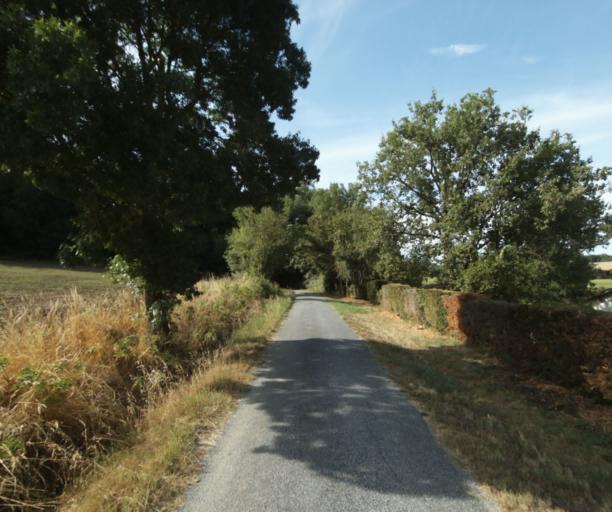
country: FR
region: Midi-Pyrenees
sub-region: Departement du Tarn
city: Soual
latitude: 43.5336
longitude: 2.0763
